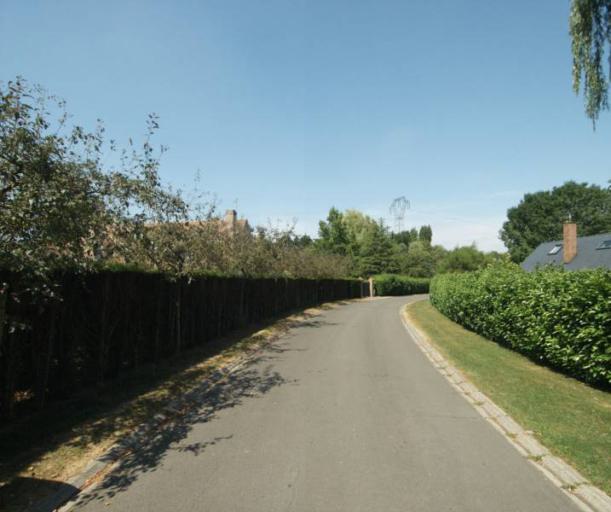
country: FR
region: Nord-Pas-de-Calais
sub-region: Departement du Nord
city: Bondues
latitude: 50.7128
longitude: 3.0803
